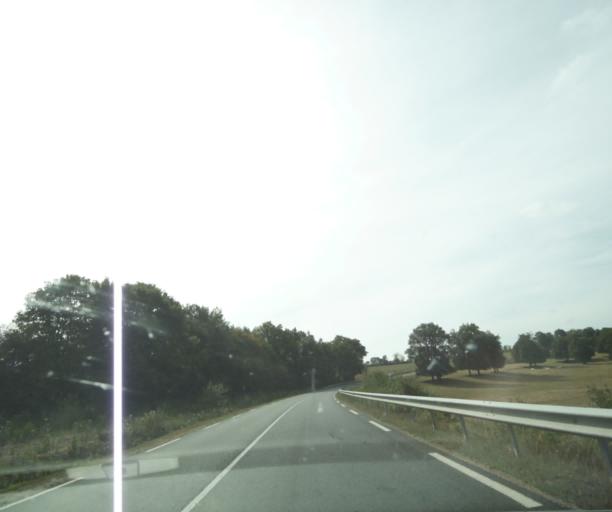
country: FR
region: Auvergne
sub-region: Departement de l'Allier
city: Lapalisse
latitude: 46.2653
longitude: 3.7284
